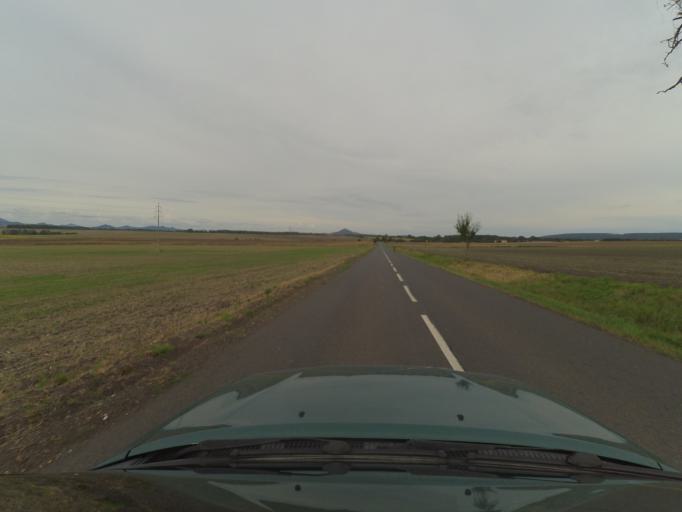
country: CZ
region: Ustecky
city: Peruc
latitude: 50.3933
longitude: 13.9158
